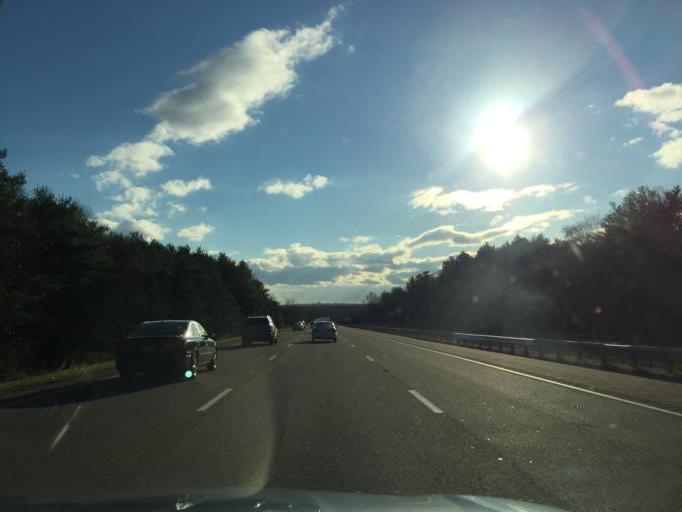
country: US
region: Massachusetts
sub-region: Bristol County
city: North Seekonk
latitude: 41.9175
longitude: -71.3337
